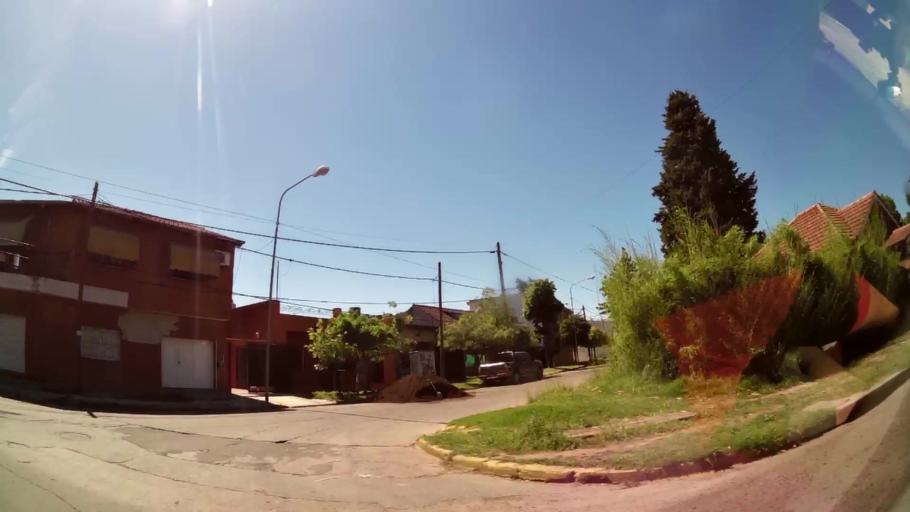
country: AR
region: Buenos Aires
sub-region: Partido de Tigre
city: Tigre
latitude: -34.4992
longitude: -58.6168
